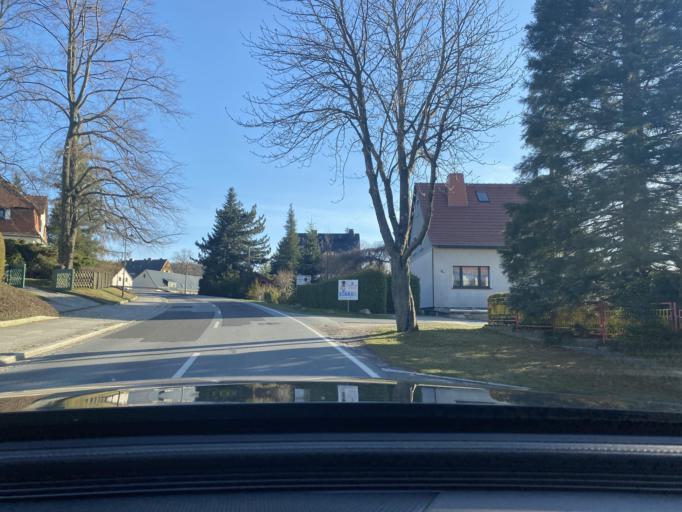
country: DE
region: Saxony
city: Sohland
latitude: 51.0425
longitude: 14.4265
